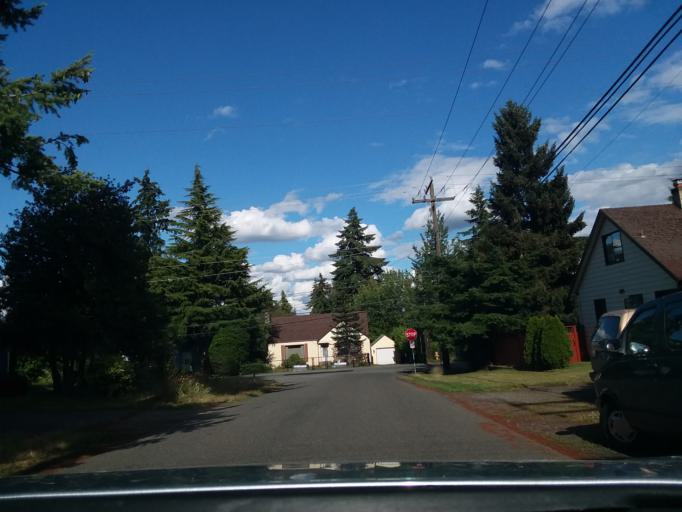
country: US
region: Washington
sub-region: King County
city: Shoreline
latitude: 47.7286
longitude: -122.3295
